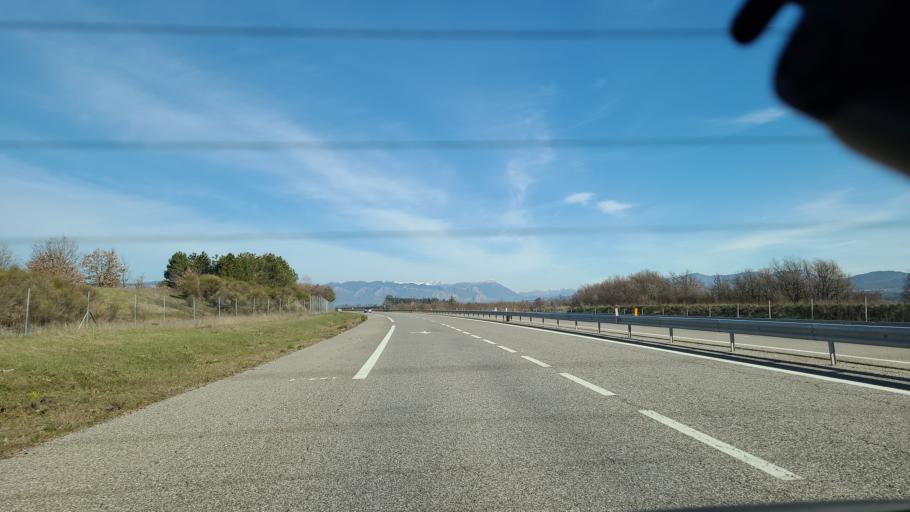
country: FR
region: Provence-Alpes-Cote d'Azur
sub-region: Departement des Alpes-de-Haute-Provence
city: Sisteron
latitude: 44.2261
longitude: 5.9187
